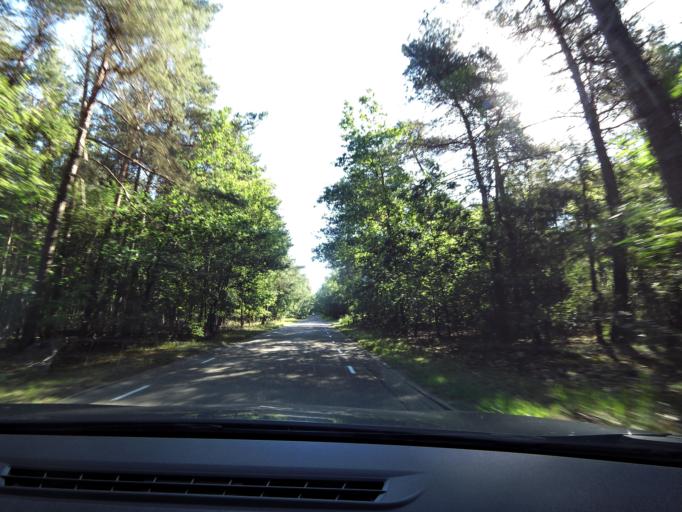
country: NL
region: Overijssel
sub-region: Gemeente Twenterand
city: Den Ham
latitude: 52.3842
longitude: 6.4248
